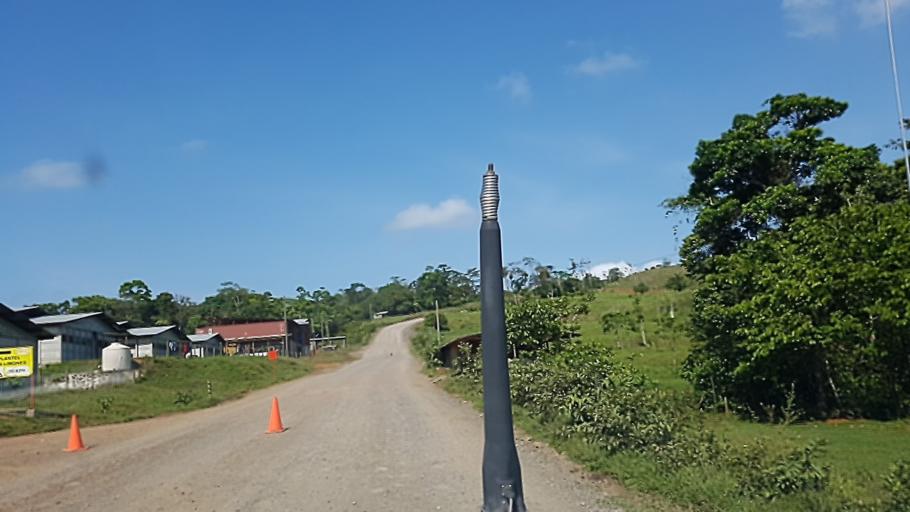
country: NI
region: Atlantico Sur
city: Nueva Guinea
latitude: 11.7894
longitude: -84.1616
